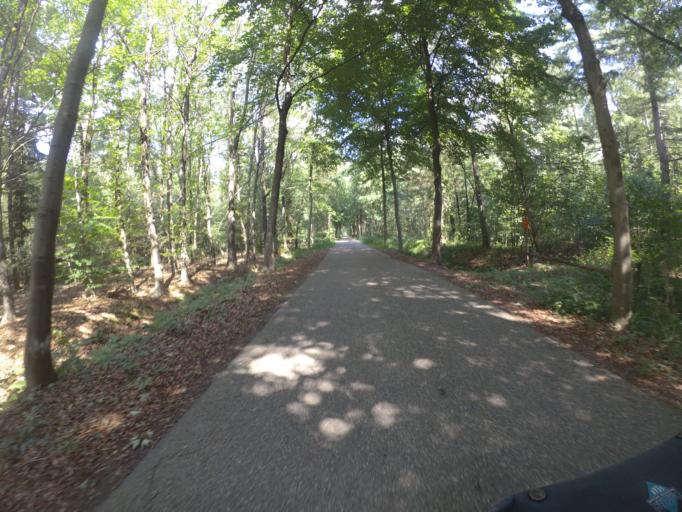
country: NL
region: North Brabant
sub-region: Gemeente Veghel
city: Eerde
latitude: 51.6240
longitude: 5.4829
